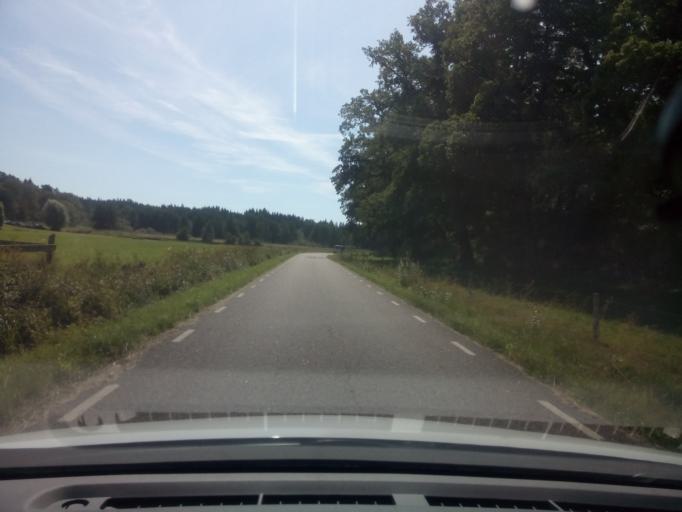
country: SE
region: Soedermanland
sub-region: Trosa Kommun
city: Trosa
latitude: 58.8076
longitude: 17.3631
